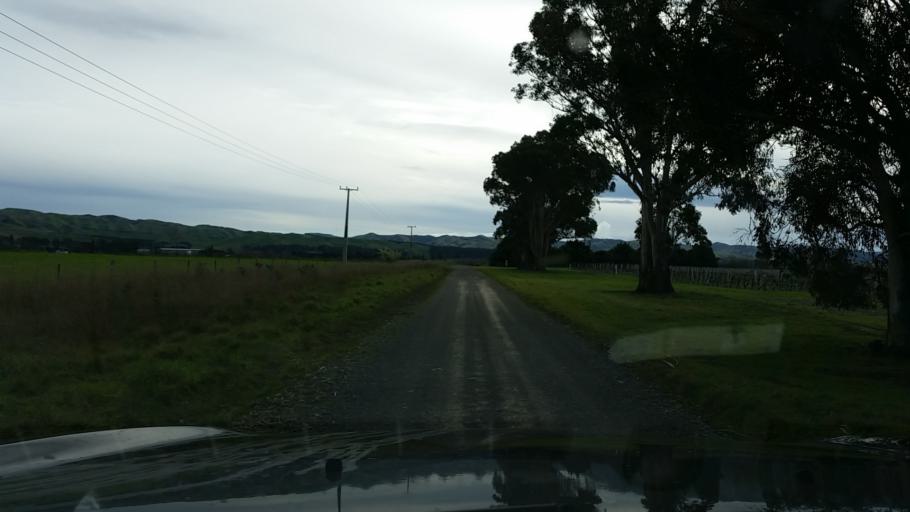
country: NZ
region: Marlborough
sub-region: Marlborough District
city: Blenheim
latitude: -41.6365
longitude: 174.1206
